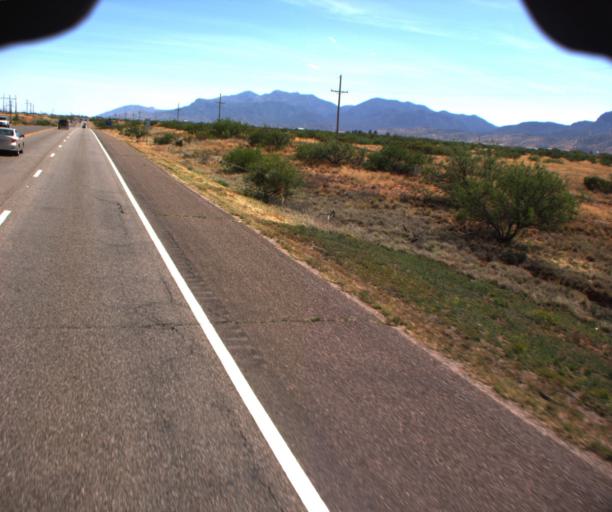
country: US
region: Arizona
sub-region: Cochise County
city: Sierra Vista
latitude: 31.5841
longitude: -110.3200
